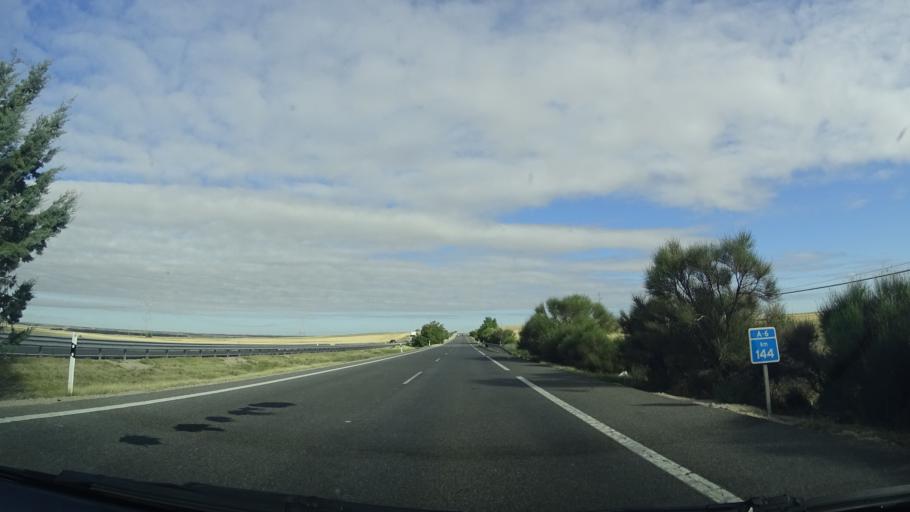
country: ES
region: Castille and Leon
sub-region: Provincia de Valladolid
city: Ataquines
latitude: 41.1994
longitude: -4.8213
